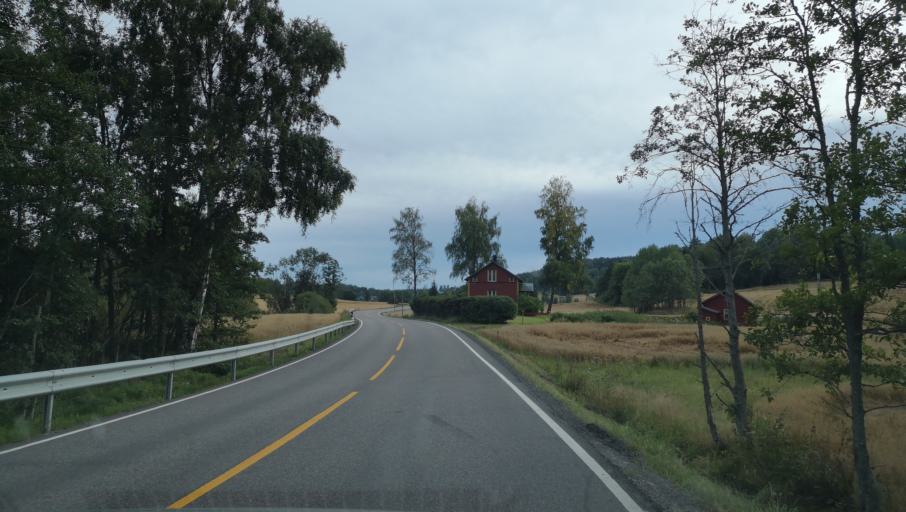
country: NO
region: Ostfold
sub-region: Hobol
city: Tomter
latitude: 59.6982
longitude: 11.0422
